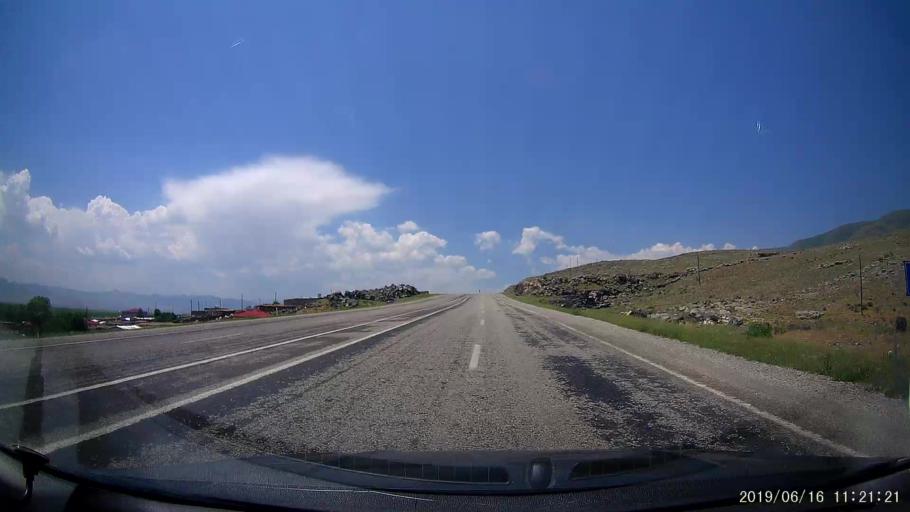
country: TR
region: Agri
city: Dogubayazit
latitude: 39.6928
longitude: 44.0728
